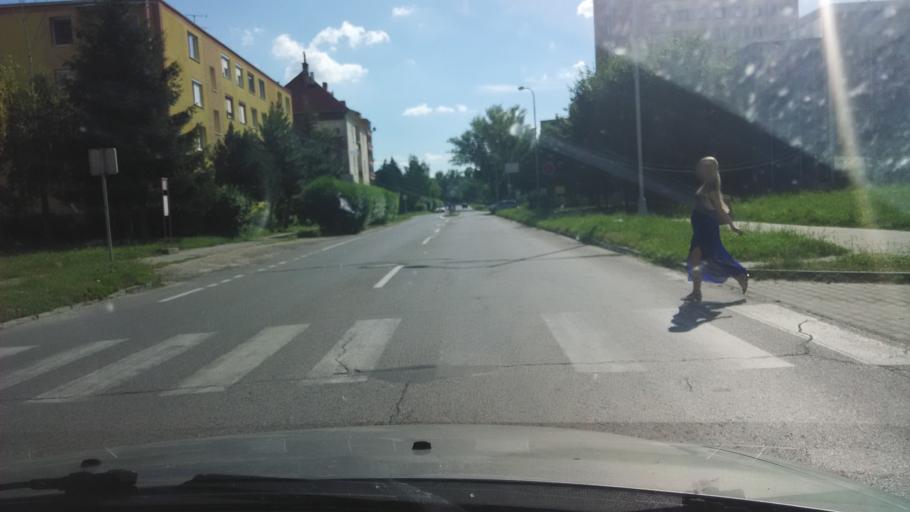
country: SK
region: Nitriansky
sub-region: Okres Nove Zamky
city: Nove Zamky
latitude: 47.9911
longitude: 18.1640
